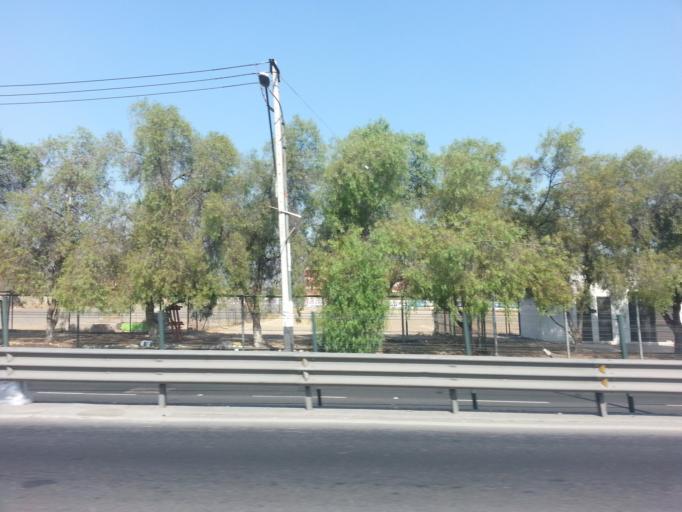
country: CL
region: Santiago Metropolitan
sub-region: Provincia de Santiago
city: La Pintana
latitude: -33.5403
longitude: -70.6504
